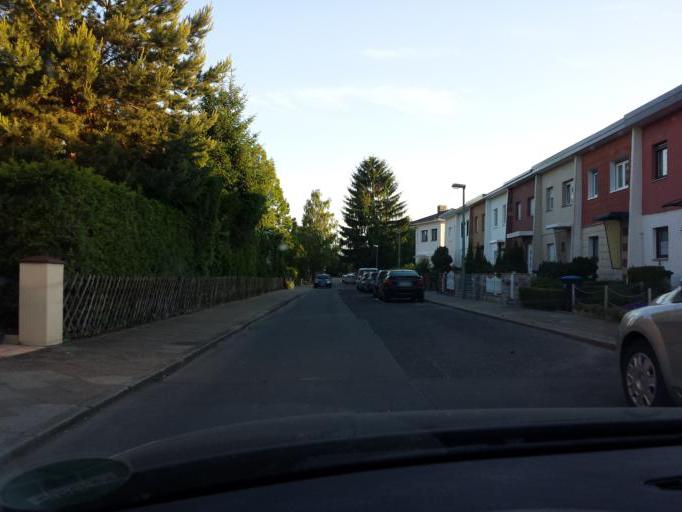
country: DE
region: Berlin
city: Lichtenrade
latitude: 52.4244
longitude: 13.4051
